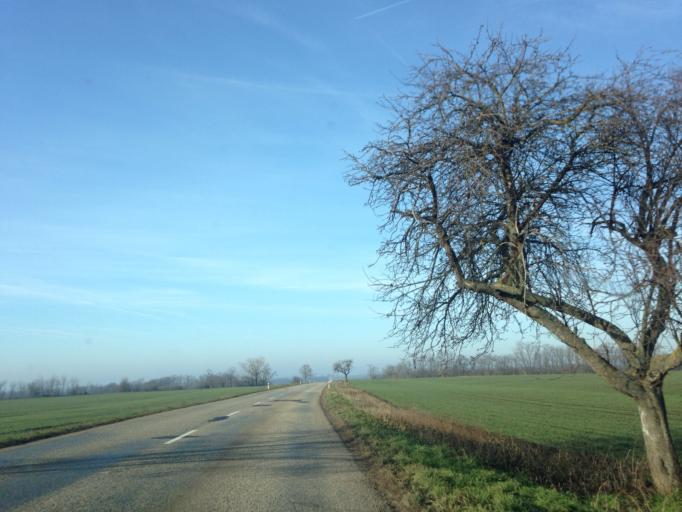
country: SK
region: Nitriansky
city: Svodin
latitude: 47.9828
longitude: 18.3695
